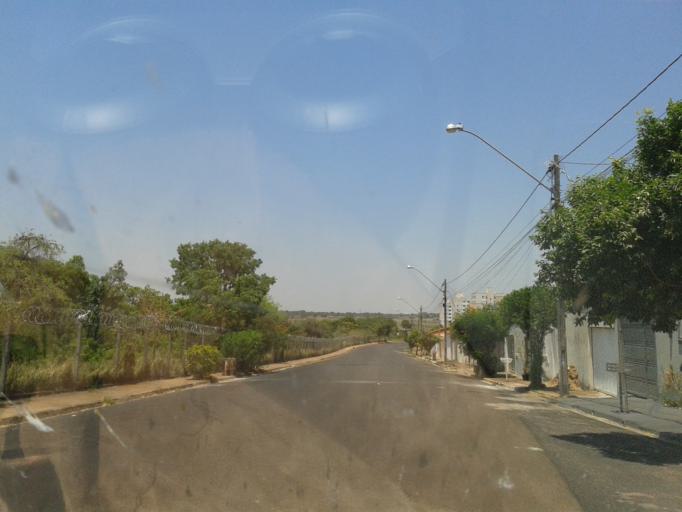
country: BR
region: Minas Gerais
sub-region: Uberlandia
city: Uberlandia
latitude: -18.9626
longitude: -48.3114
